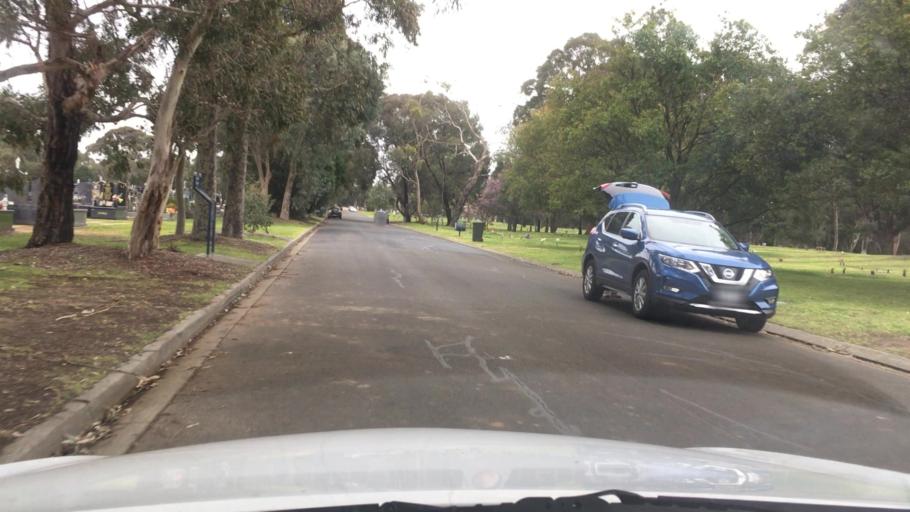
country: AU
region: Victoria
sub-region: Greater Dandenong
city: Noble Park North
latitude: -37.9438
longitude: 145.1856
